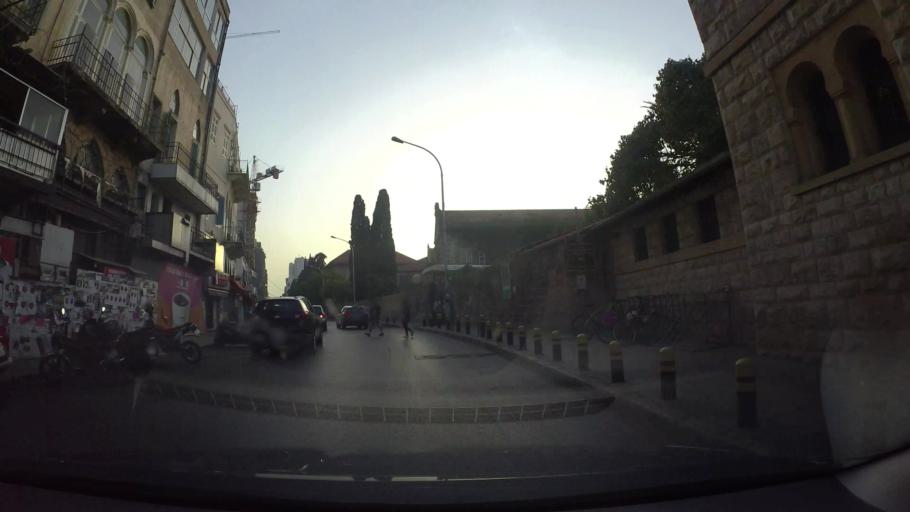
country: LB
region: Beyrouth
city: Ra's Bayrut
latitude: 33.8995
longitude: 35.4822
